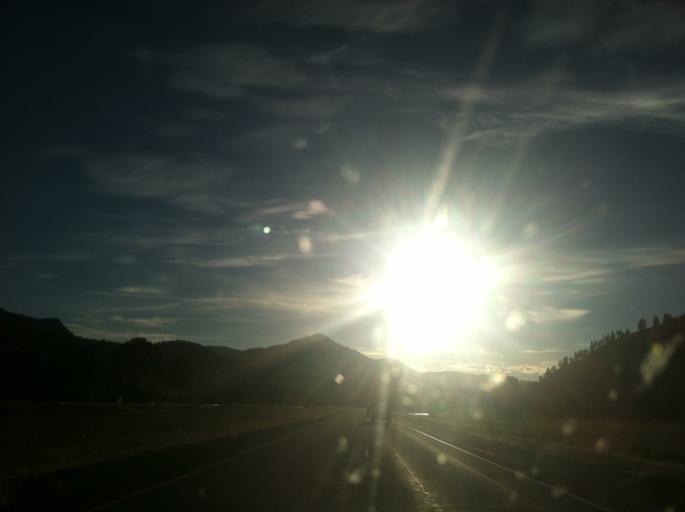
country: US
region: Montana
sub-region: Missoula County
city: Clinton
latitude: 46.6980
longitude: -113.3986
